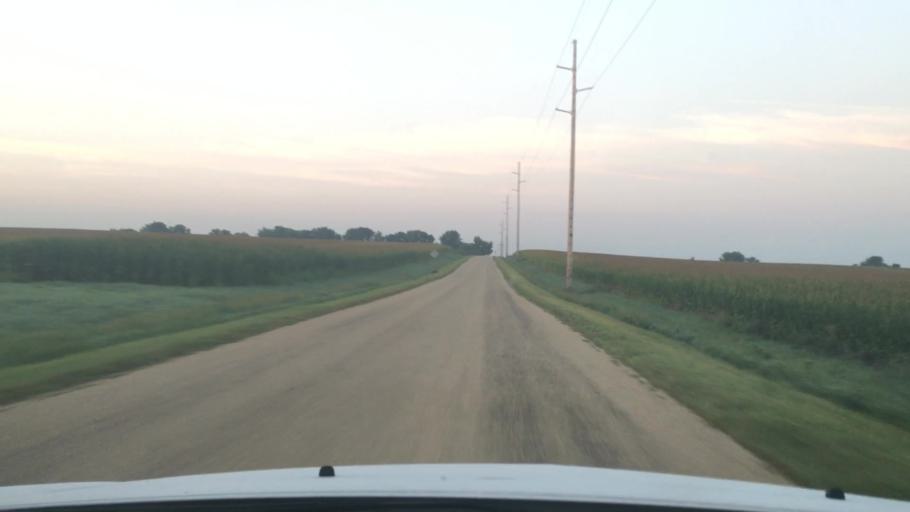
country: US
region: Illinois
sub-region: Ogle County
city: Rochelle
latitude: 41.8892
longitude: -89.0009
